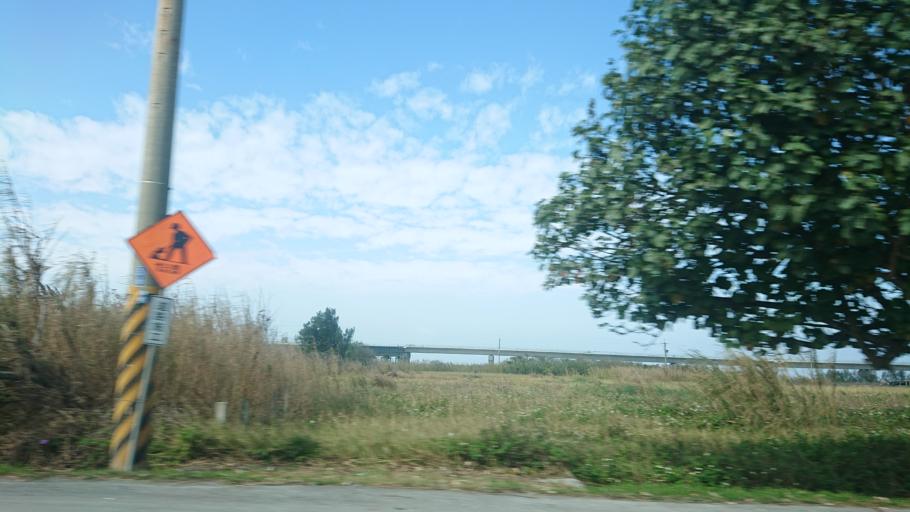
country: TW
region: Taiwan
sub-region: Changhua
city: Chang-hua
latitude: 23.9068
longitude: 120.3086
